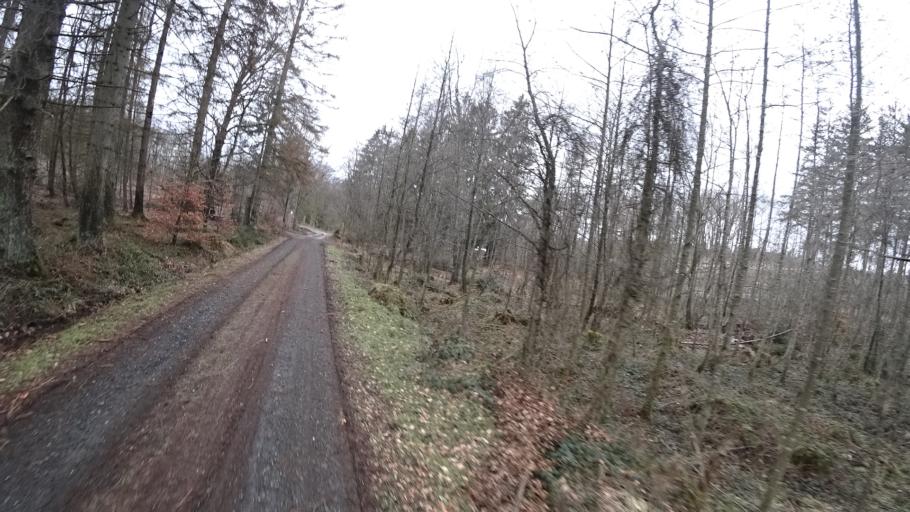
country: DE
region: Rheinland-Pfalz
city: Ransbach-Baumbach
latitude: 50.4414
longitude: 7.7208
